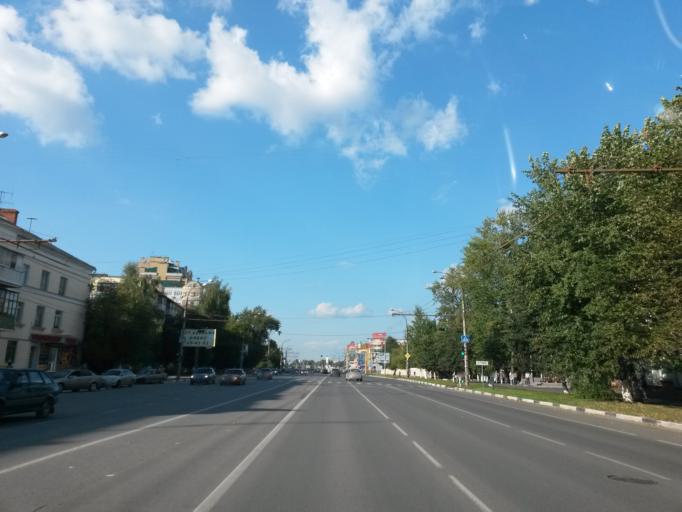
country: RU
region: Ivanovo
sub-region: Gorod Ivanovo
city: Ivanovo
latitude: 56.9787
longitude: 40.9777
